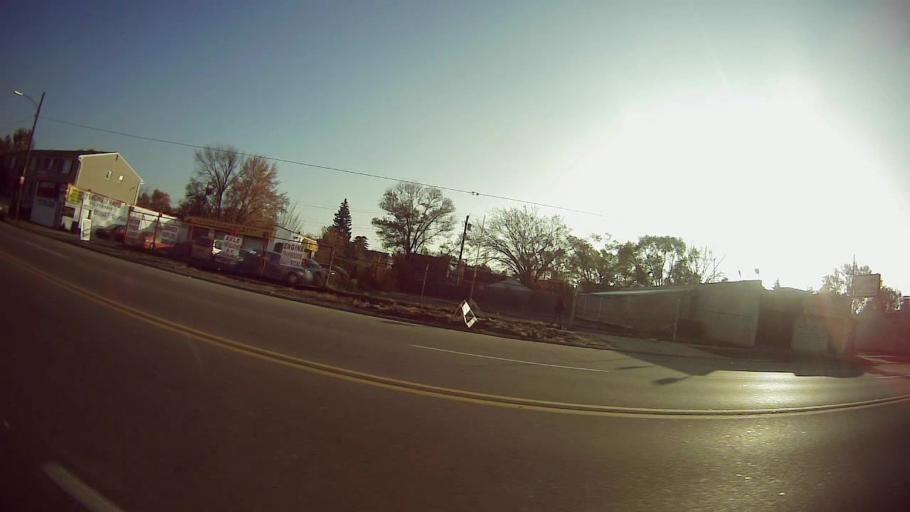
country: US
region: Michigan
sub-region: Wayne County
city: Dearborn
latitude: 42.3607
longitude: -83.1971
